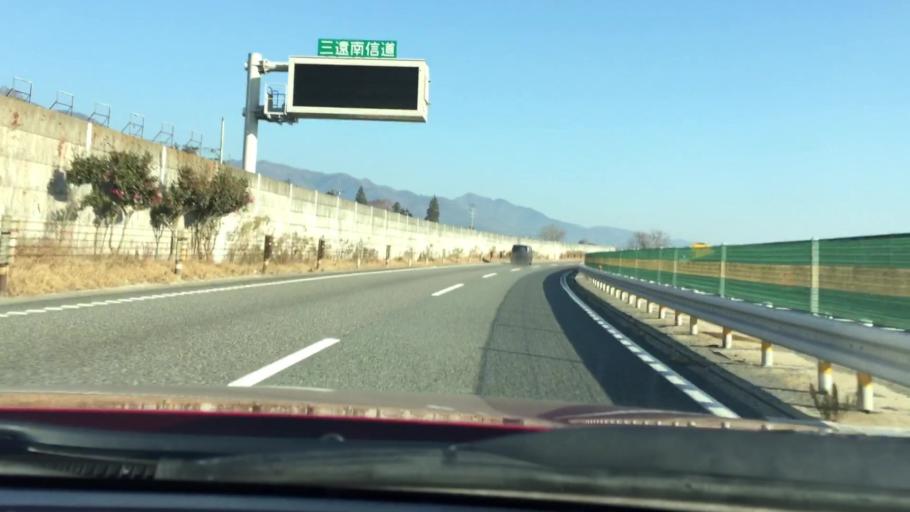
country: JP
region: Nagano
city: Iida
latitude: 35.4619
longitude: 137.7531
